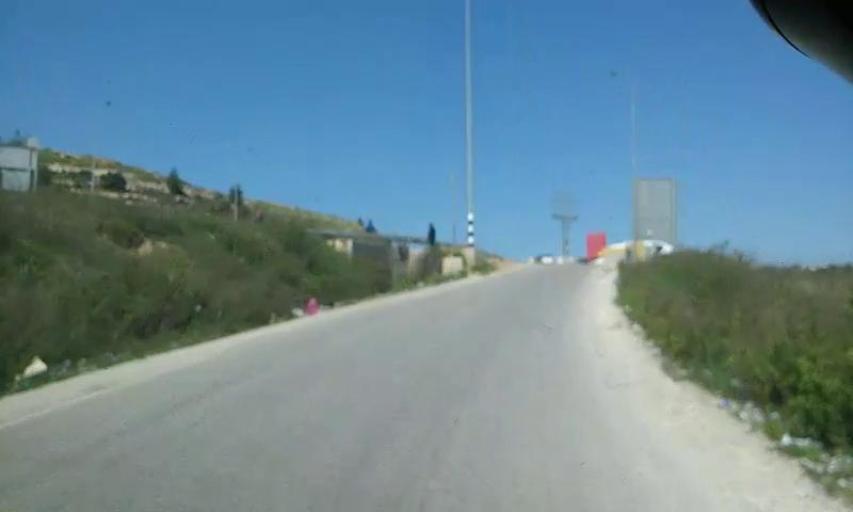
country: PS
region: West Bank
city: Al Khadir
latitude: 31.7050
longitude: 35.1565
